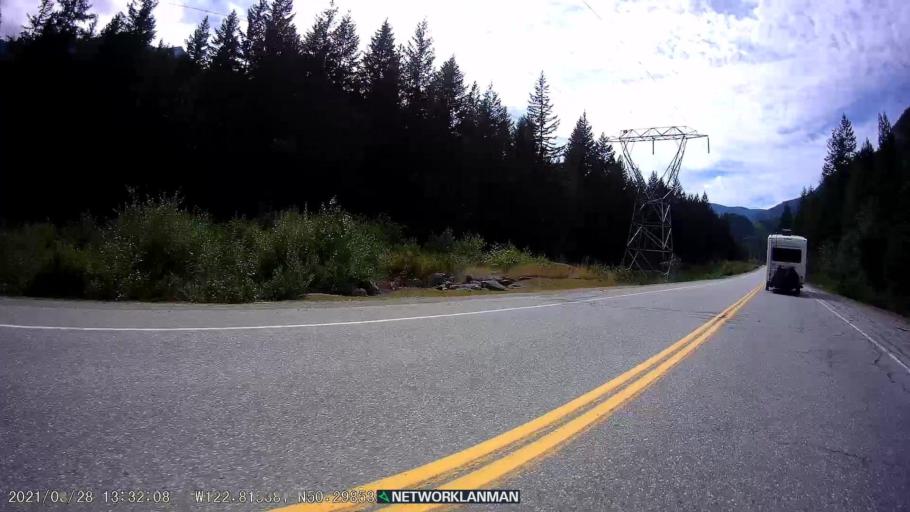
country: CA
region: British Columbia
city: Pemberton
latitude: 50.2982
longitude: -122.8166
